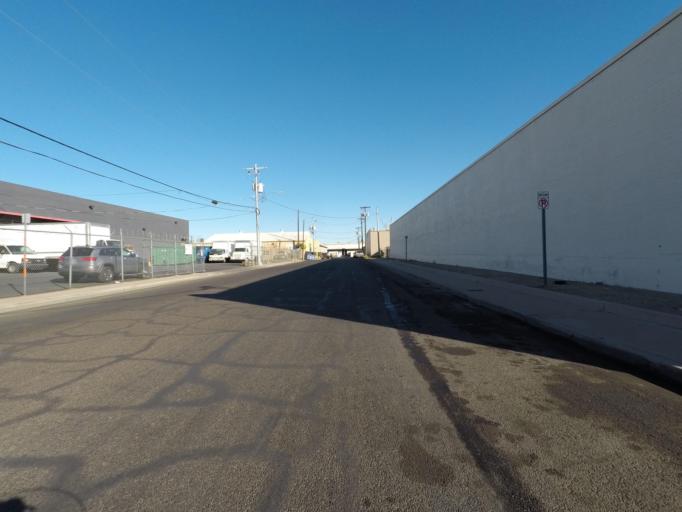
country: US
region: Arizona
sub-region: Maricopa County
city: Phoenix
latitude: 33.4696
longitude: -112.1082
